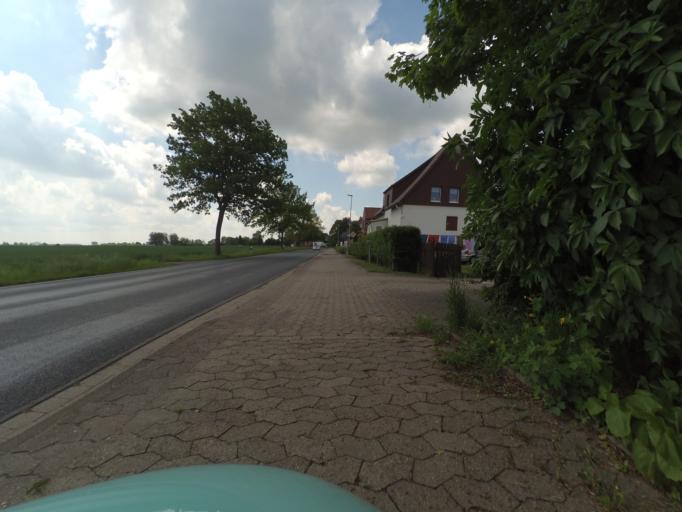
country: DE
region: Lower Saxony
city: Lengede
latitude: 52.2598
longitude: 10.2795
